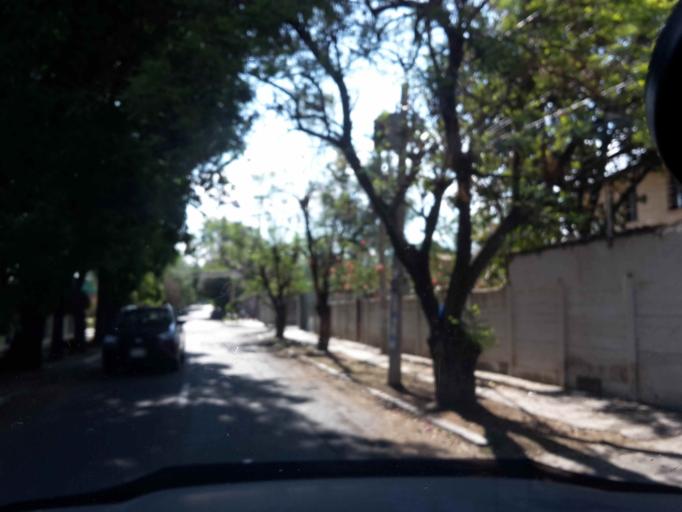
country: BO
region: Cochabamba
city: Cochabamba
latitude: -17.3737
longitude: -66.1703
